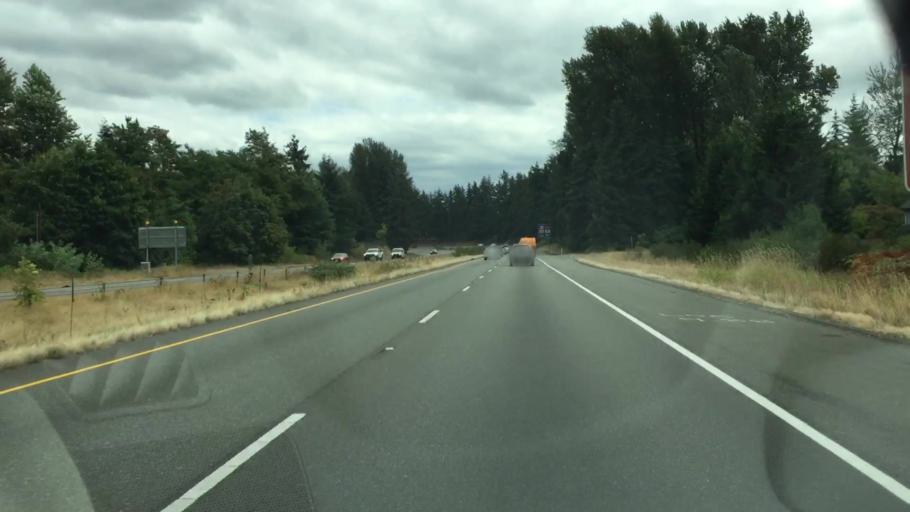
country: US
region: Washington
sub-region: Pierce County
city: Sumner
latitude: 47.1933
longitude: -122.2396
